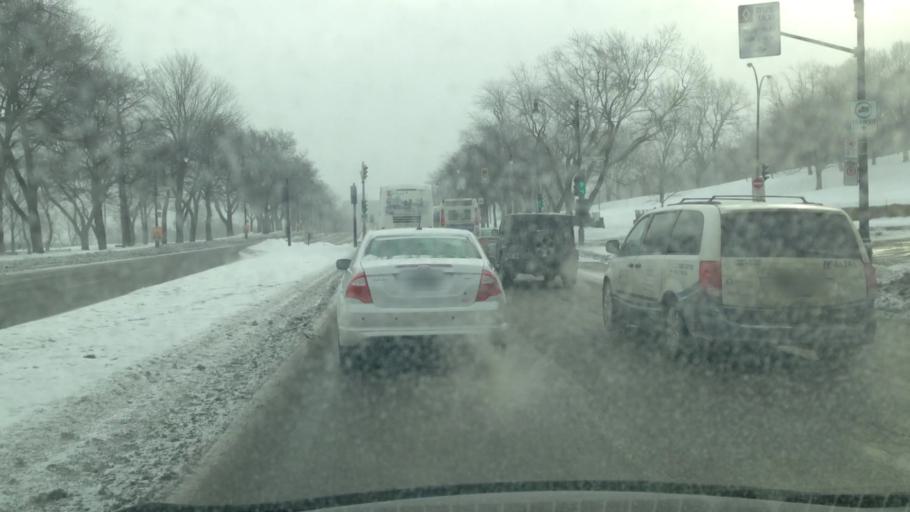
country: CA
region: Quebec
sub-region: Montreal
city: Montreal
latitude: 45.5166
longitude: -73.5890
